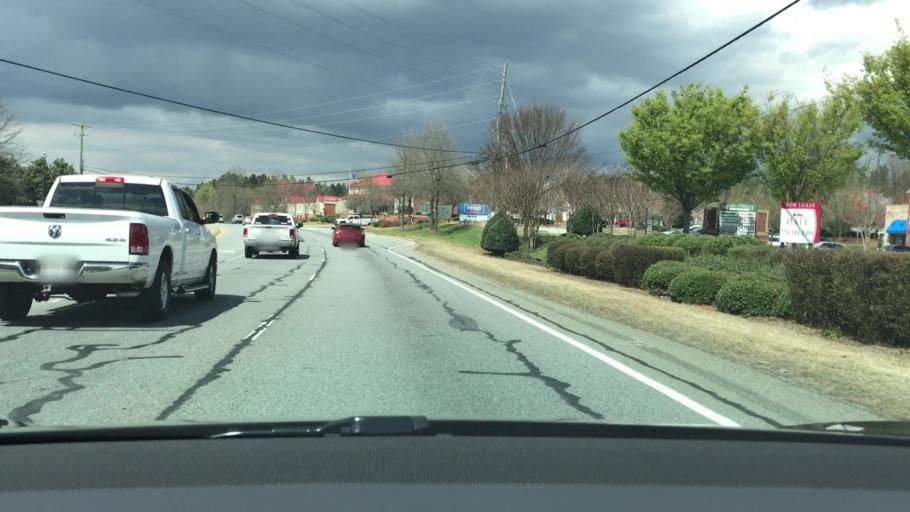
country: US
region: Georgia
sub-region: Gwinnett County
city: Suwanee
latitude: 34.0434
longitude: -84.0547
